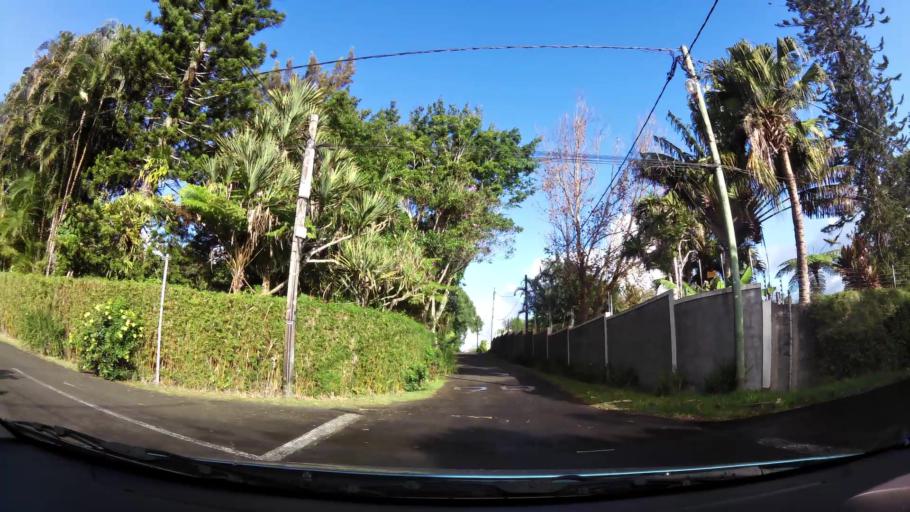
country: MU
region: Plaines Wilhems
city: Curepipe
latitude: -20.3176
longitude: 57.5044
